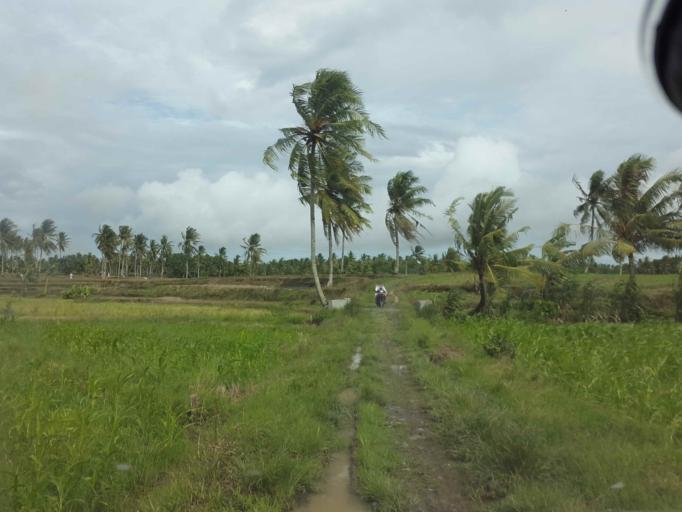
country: ID
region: Lampung
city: Palas
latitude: -5.6260
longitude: 105.6439
